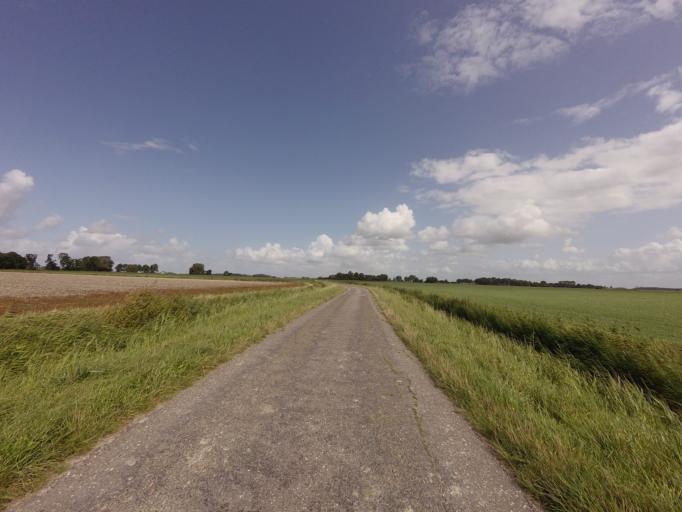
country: NL
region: Friesland
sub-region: Gemeente Harlingen
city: Harlingen
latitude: 53.1195
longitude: 5.4394
